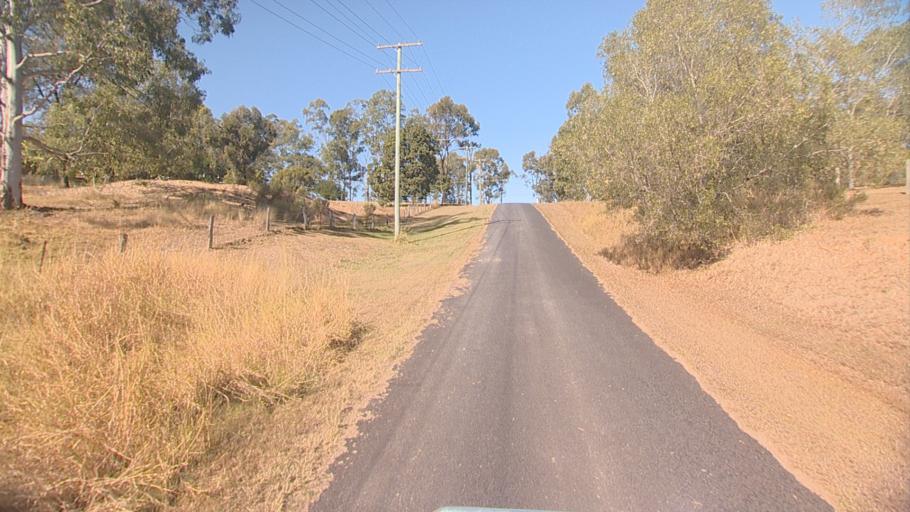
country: AU
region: Queensland
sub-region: Logan
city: Cedar Vale
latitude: -27.9000
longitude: 153.0220
